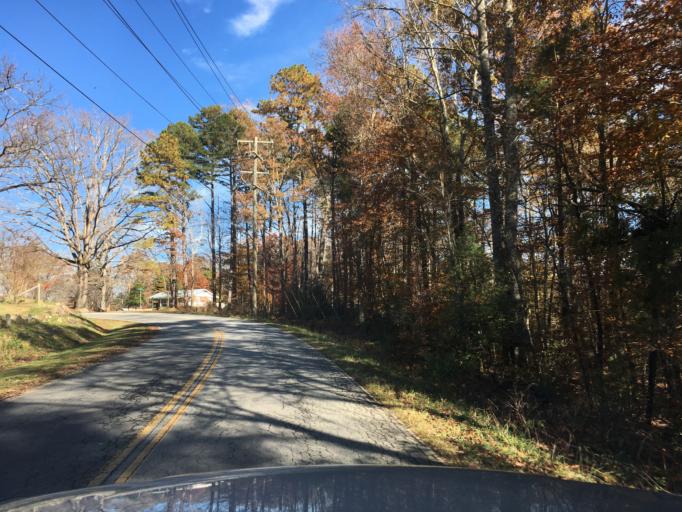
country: US
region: North Carolina
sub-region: Henderson County
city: Etowah
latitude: 35.3141
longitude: -82.6204
